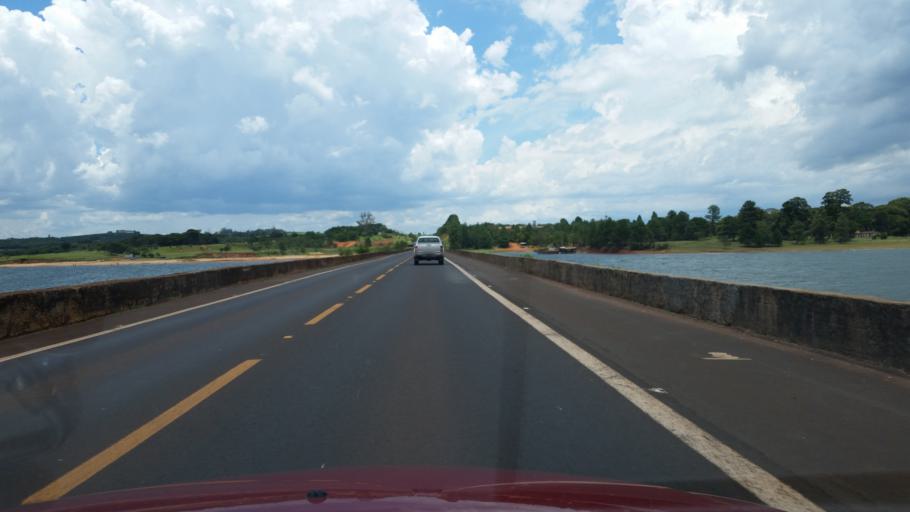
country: BR
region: Sao Paulo
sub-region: Itai
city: Itai
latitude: -23.2703
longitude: -49.0124
